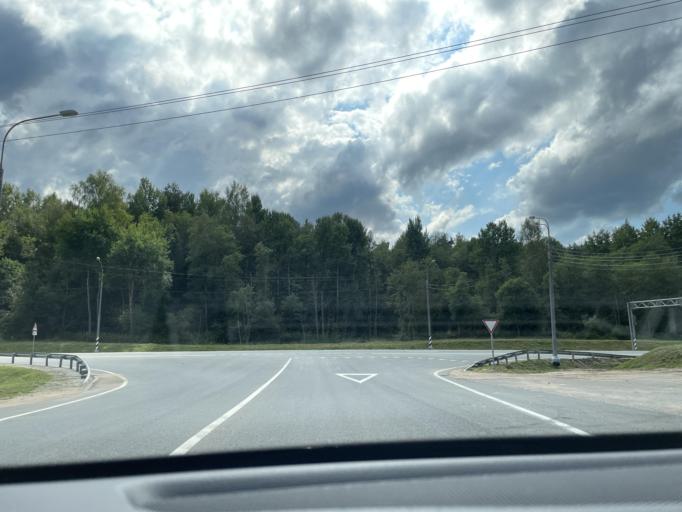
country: RU
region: Novgorod
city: Valday
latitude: 57.9985
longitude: 33.1613
